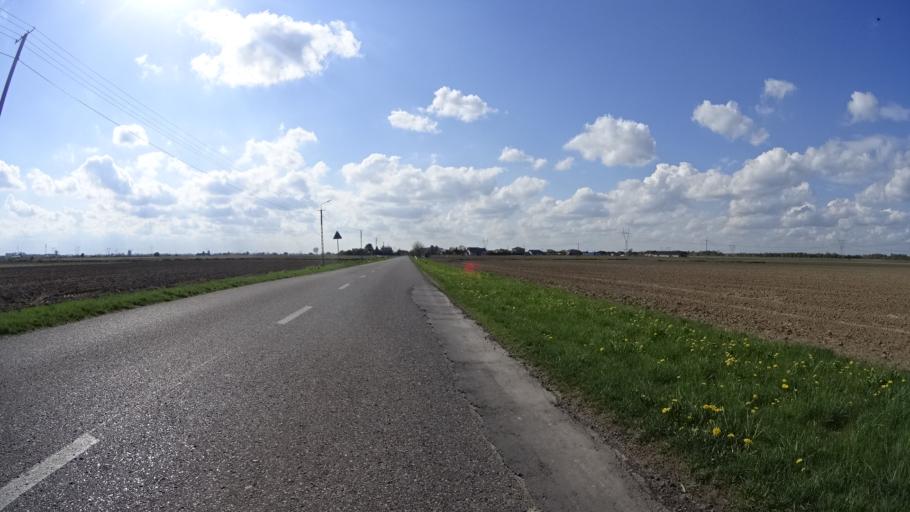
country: PL
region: Masovian Voivodeship
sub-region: Powiat warszawski zachodni
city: Jozefow
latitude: 52.2330
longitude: 20.6839
